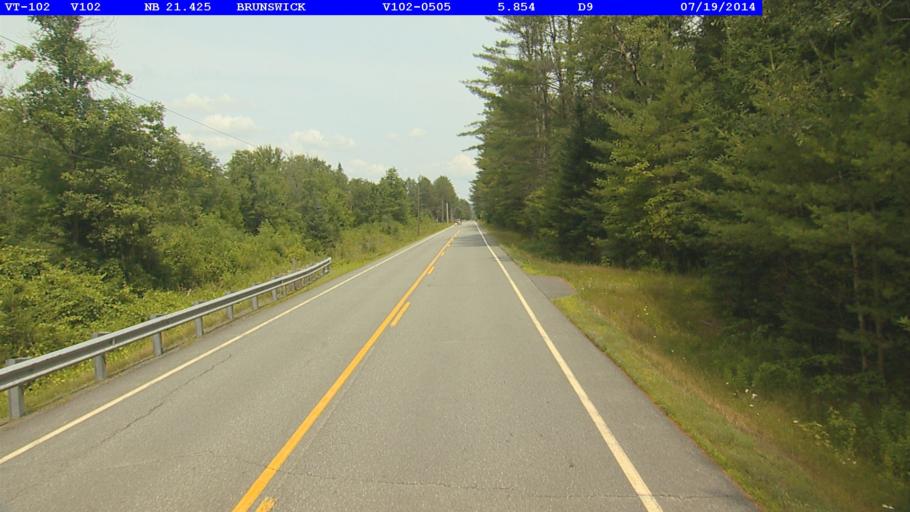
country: US
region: New Hampshire
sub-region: Coos County
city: Stratford
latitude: 44.7319
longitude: -71.6350
